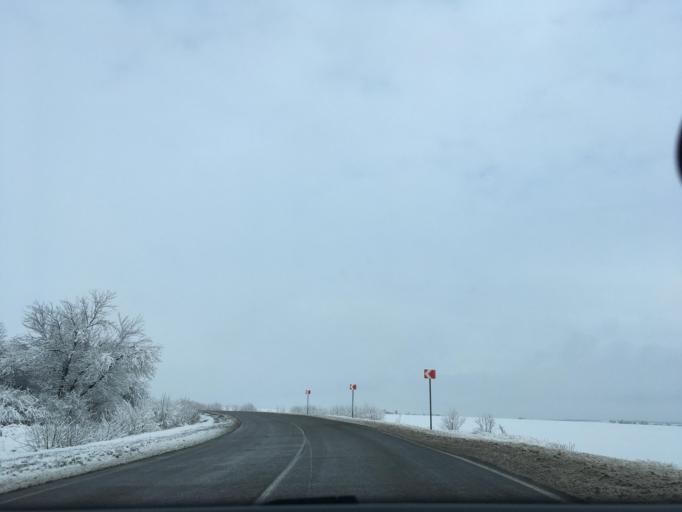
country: UA
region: Luhansk
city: Lozno-Oleksandrivka
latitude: 49.9974
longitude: 39.0406
